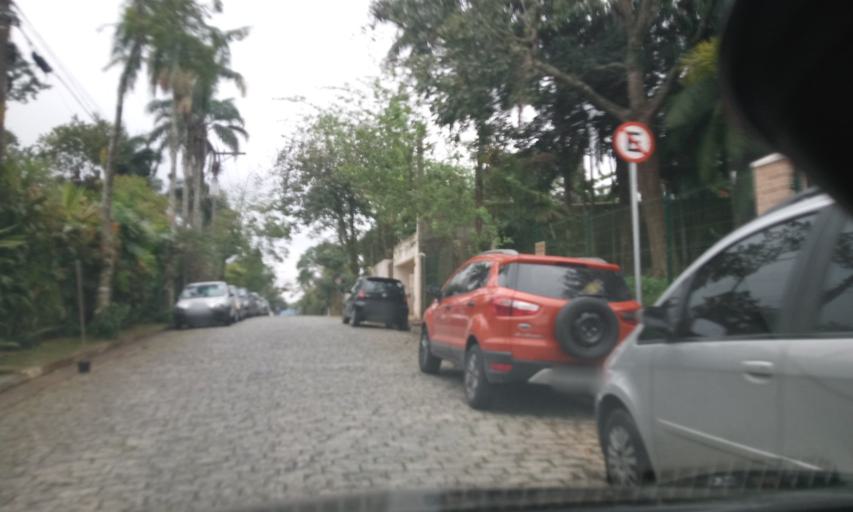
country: BR
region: Sao Paulo
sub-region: Sao Bernardo Do Campo
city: Sao Bernardo do Campo
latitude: -23.7801
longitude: -46.5364
